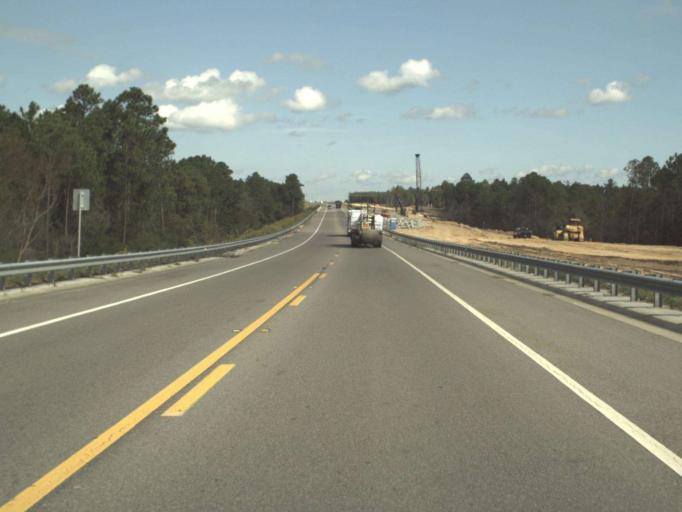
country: US
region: Florida
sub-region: Walton County
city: Freeport
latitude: 30.5220
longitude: -86.1086
